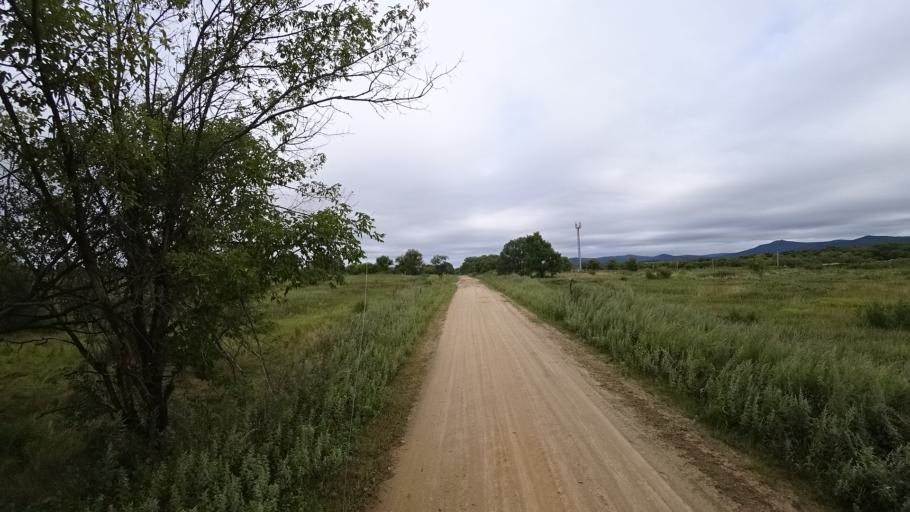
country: RU
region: Primorskiy
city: Rettikhovka
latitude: 44.1297
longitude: 132.6380
